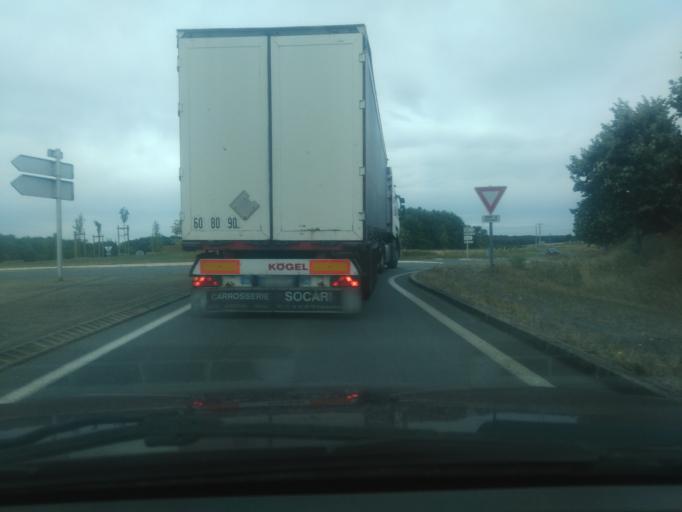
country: FR
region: Poitou-Charentes
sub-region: Departement de la Vienne
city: Chauvigny
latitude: 46.5626
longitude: 0.6183
